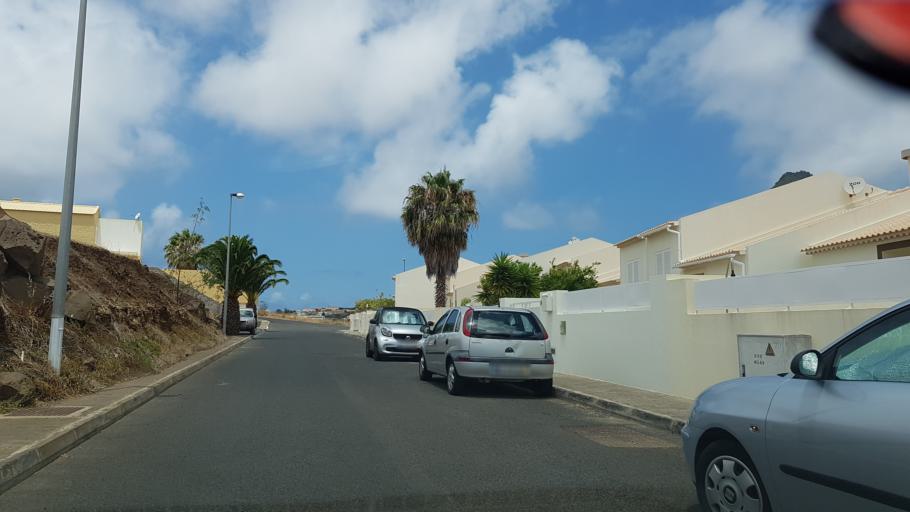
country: PT
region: Madeira
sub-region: Porto Santo
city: Vila de Porto Santo
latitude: 33.0632
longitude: -16.3372
